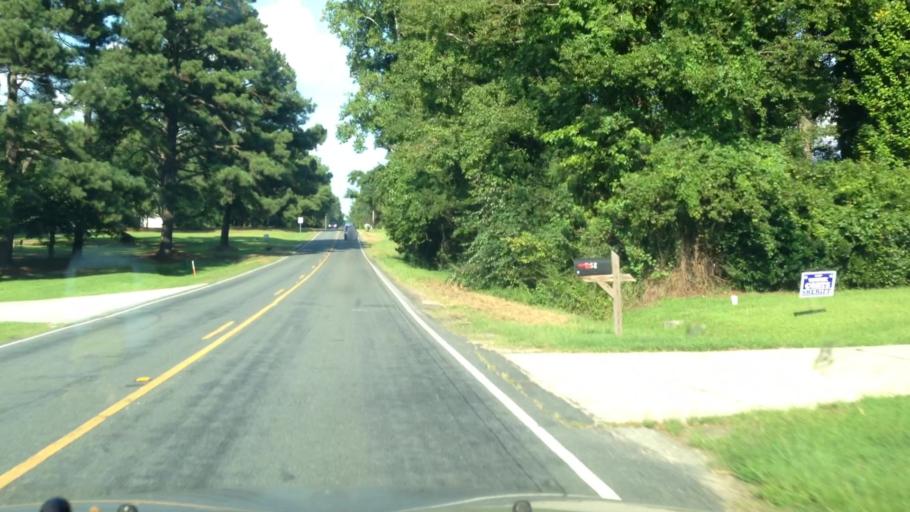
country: US
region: North Carolina
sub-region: Harnett County
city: Buies Creek
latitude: 35.4116
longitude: -78.7224
